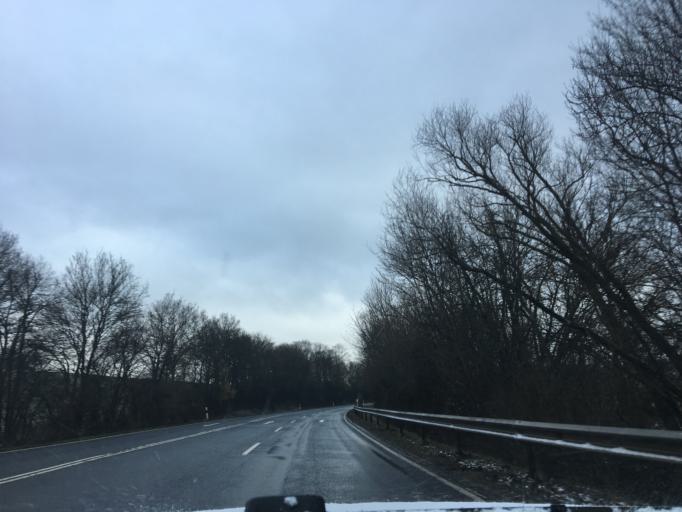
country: DE
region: Rheinland-Pfalz
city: Orbis
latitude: 49.6845
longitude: 8.0080
